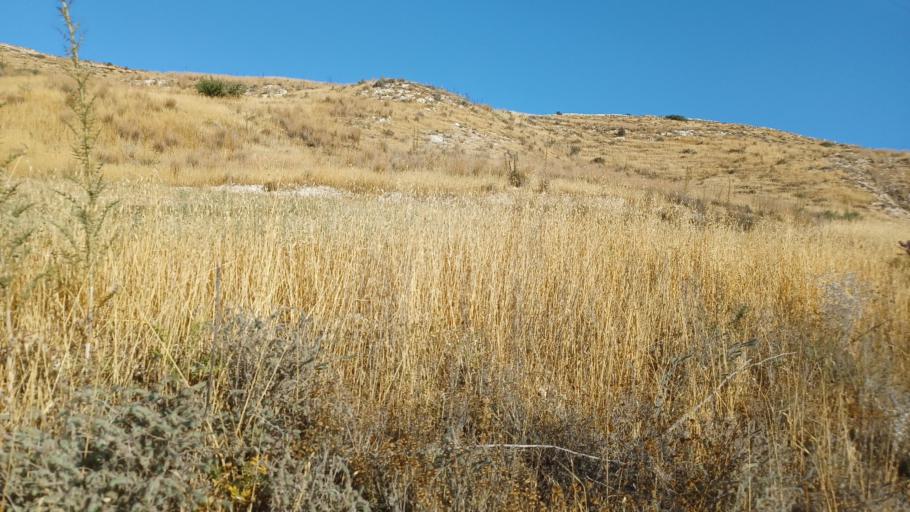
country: CY
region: Larnaka
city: Troulloi
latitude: 35.0256
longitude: 33.5756
